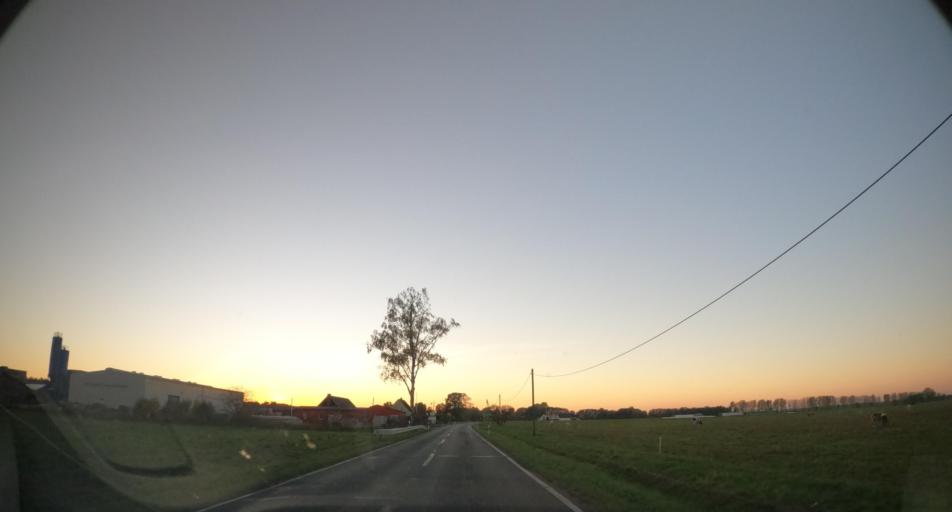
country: DE
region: Mecklenburg-Vorpommern
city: Ducherow
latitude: 53.7787
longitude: 13.8779
